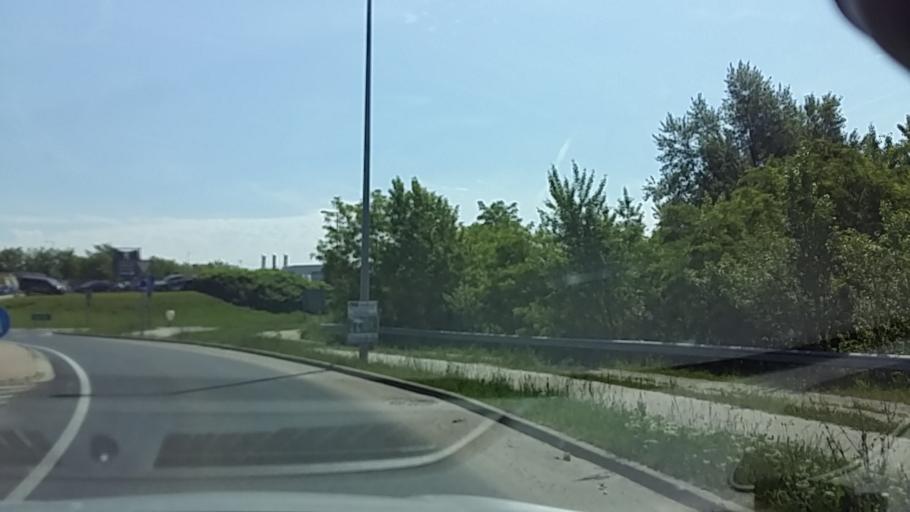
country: HU
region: Gyor-Moson-Sopron
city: Sopron
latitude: 47.6819
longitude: 16.6130
